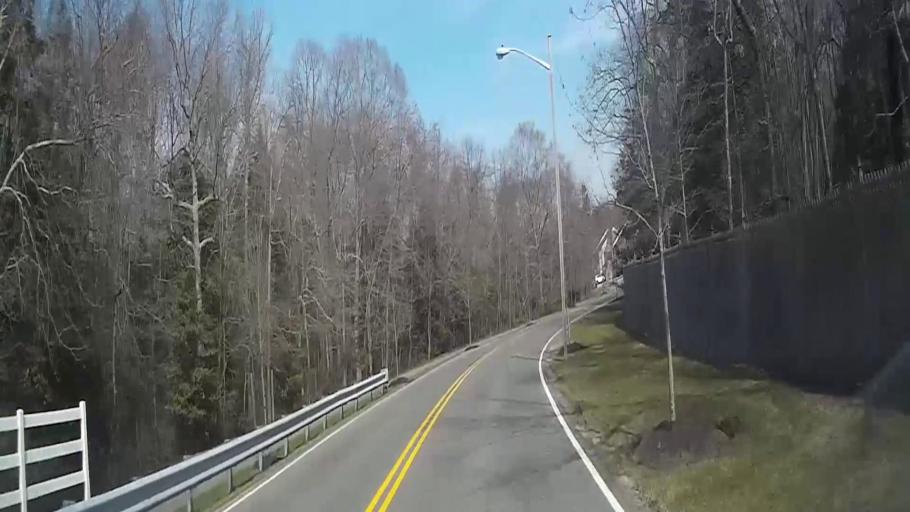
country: US
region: New Jersey
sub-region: Burlington County
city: Marlton
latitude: 39.8633
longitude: -74.8733
